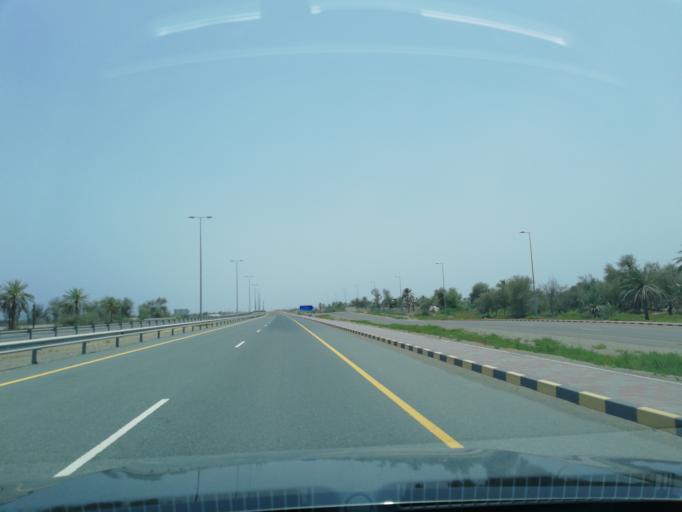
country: OM
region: Al Batinah
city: Shinas
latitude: 24.7725
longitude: 56.4588
